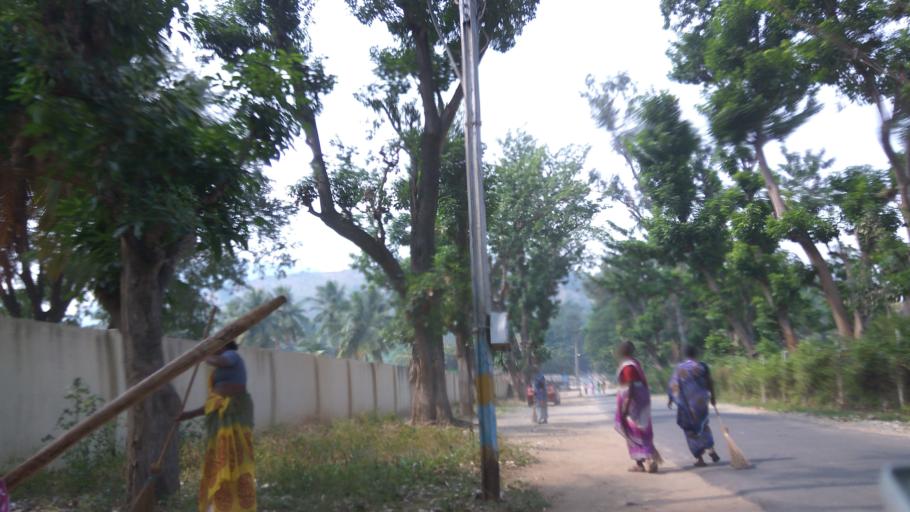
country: IN
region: Tamil Nadu
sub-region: Krishnagiri
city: Krishnagiri
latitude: 12.4741
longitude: 78.1866
